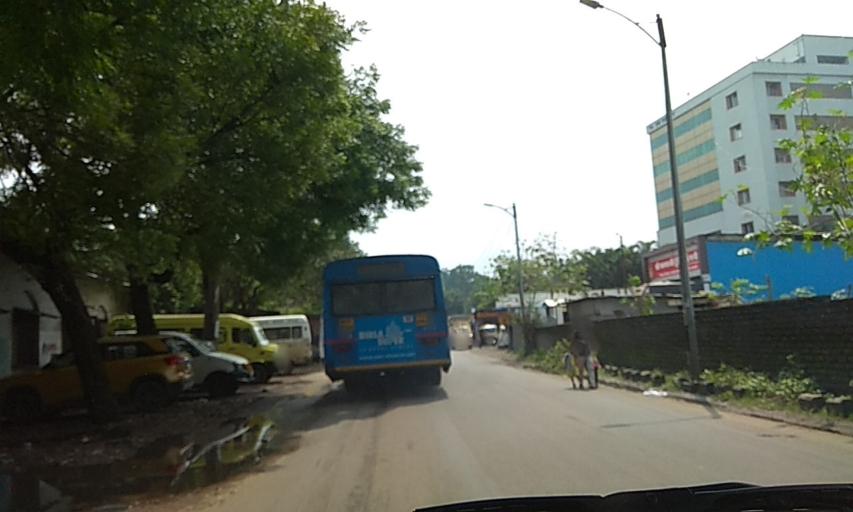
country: IN
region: Maharashtra
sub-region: Pune Division
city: Shivaji Nagar
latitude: 18.5381
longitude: 73.7940
